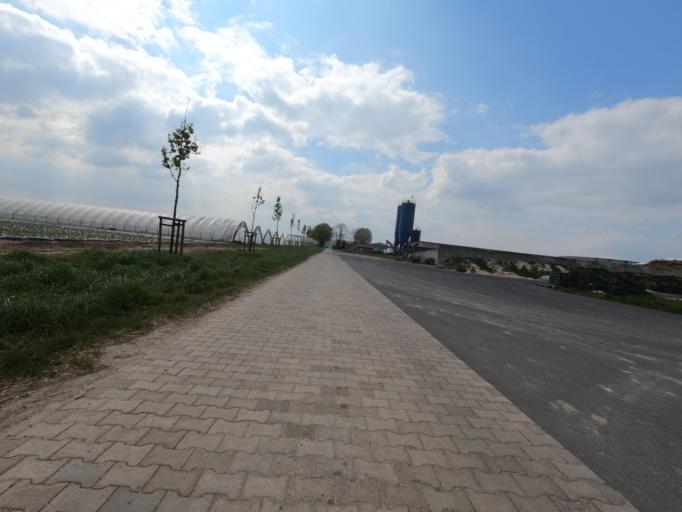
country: DE
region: North Rhine-Westphalia
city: Huckelhoven
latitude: 51.0868
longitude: 6.2290
